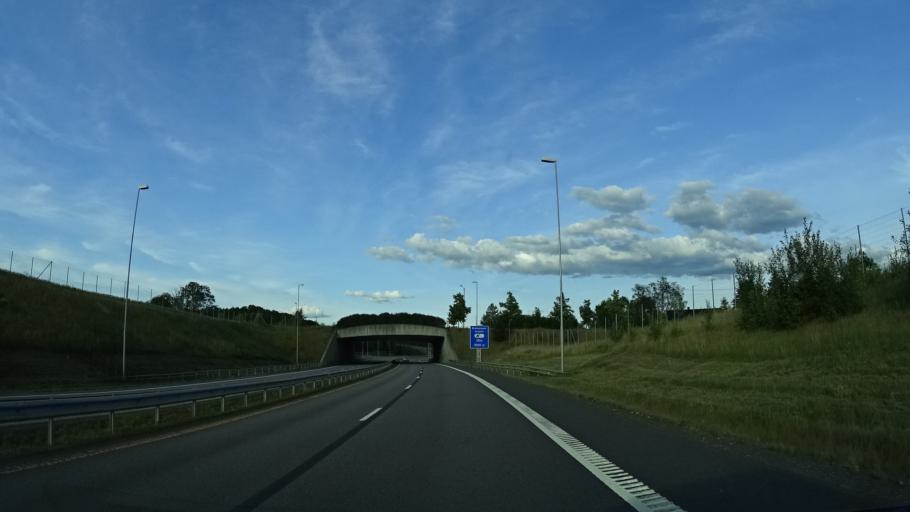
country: NO
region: Ostfold
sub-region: Eidsberg
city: Mysen
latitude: 59.5764
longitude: 11.2569
